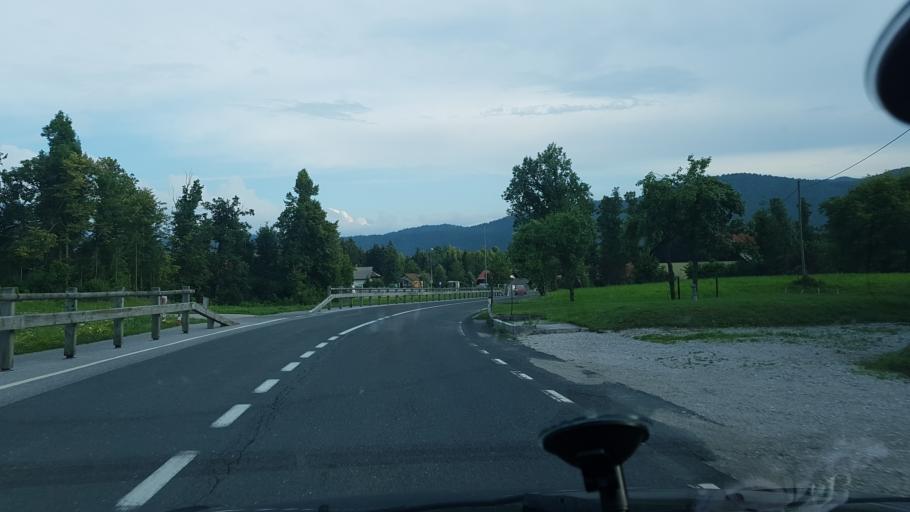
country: SI
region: Logatec
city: Logatec
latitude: 45.9222
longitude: 14.1415
